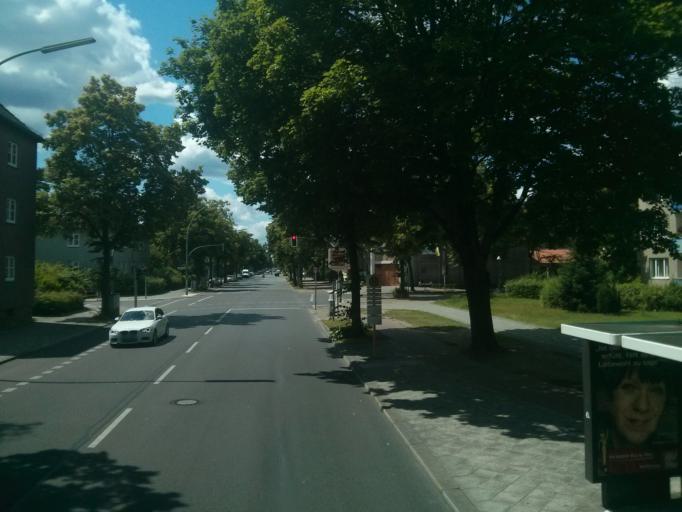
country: DE
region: Berlin
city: Tegel
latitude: 52.5757
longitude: 13.2859
